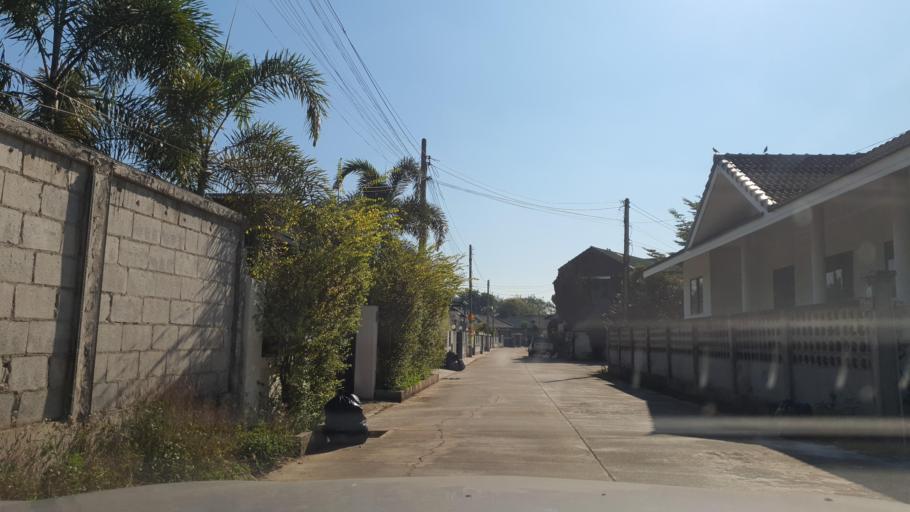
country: TH
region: Chiang Mai
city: Hang Dong
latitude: 18.6942
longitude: 98.9358
